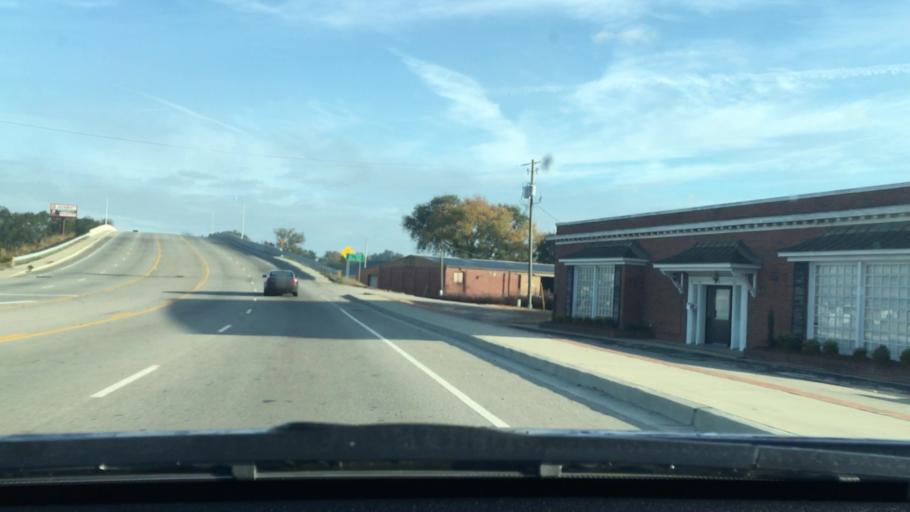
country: US
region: South Carolina
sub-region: Sumter County
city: Sumter
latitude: 33.9143
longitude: -80.3366
